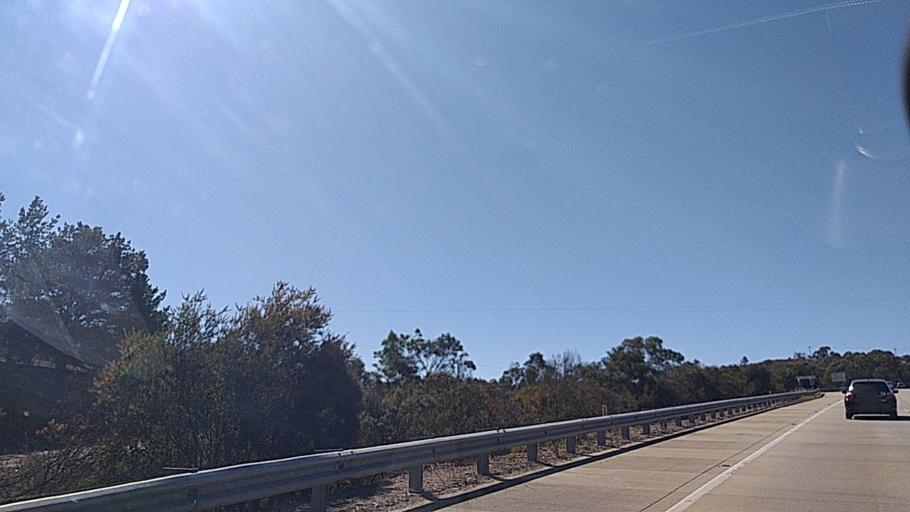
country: AU
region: New South Wales
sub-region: Yass Valley
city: Gundaroo
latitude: -35.1640
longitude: 149.3104
